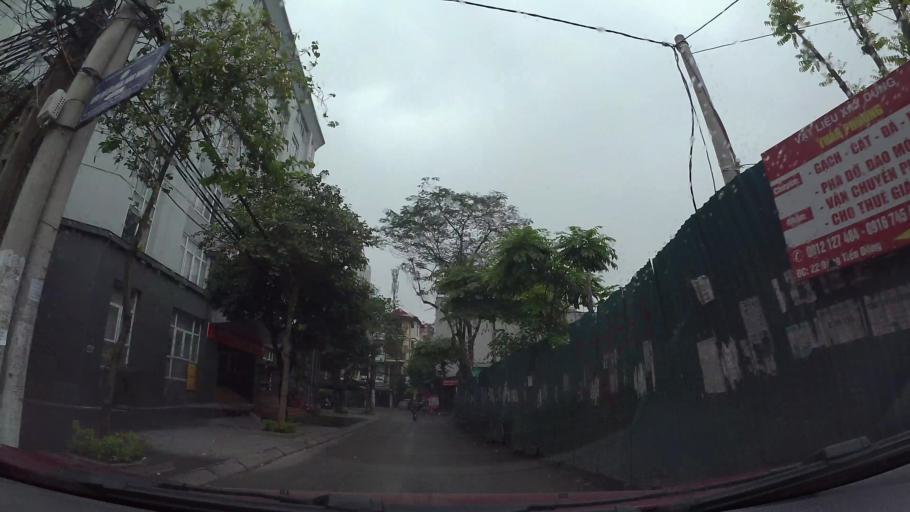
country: VN
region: Ha Noi
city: Dong Da
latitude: 21.0143
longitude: 105.8218
